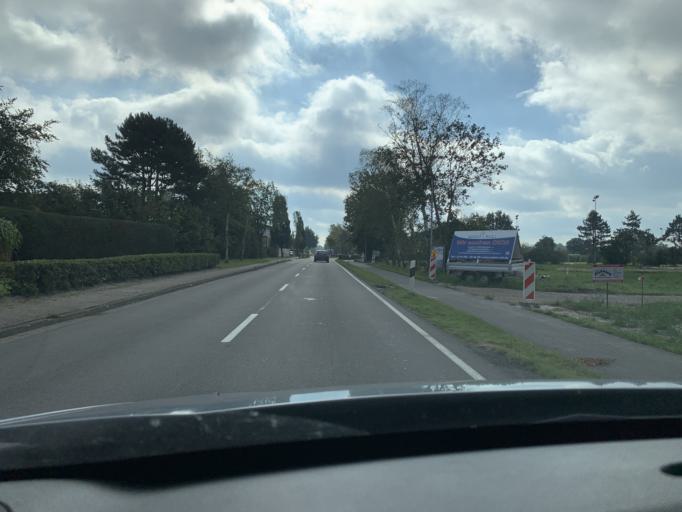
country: DE
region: Lower Saxony
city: Edewecht
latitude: 53.1013
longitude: 8.0778
